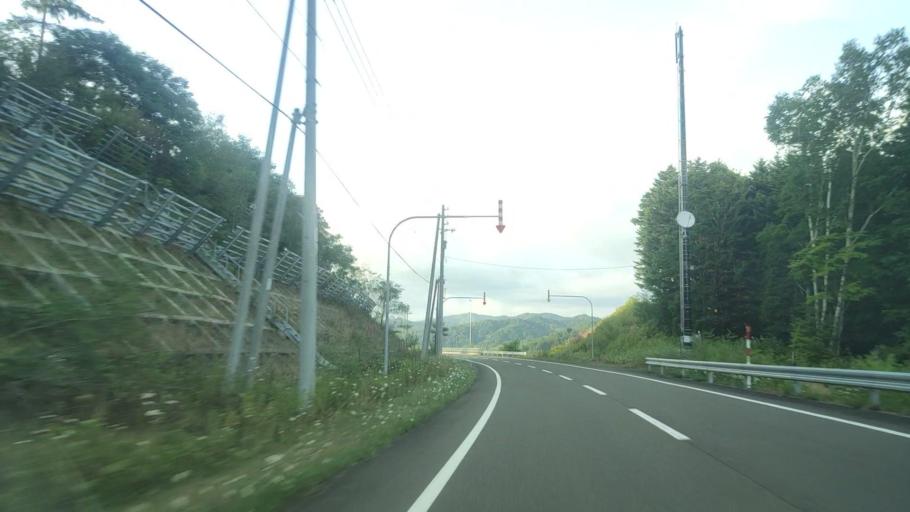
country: JP
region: Hokkaido
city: Bibai
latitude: 43.0684
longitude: 142.1038
